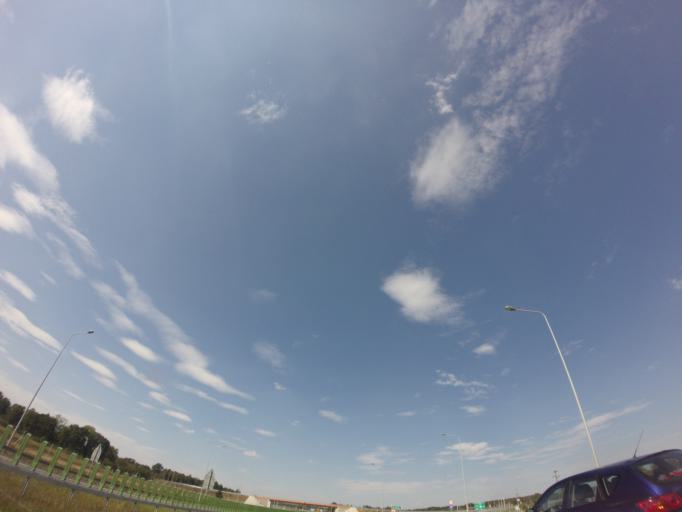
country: PL
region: Lower Silesian Voivodeship
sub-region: Legnica
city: Legnica
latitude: 51.2661
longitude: 16.1532
